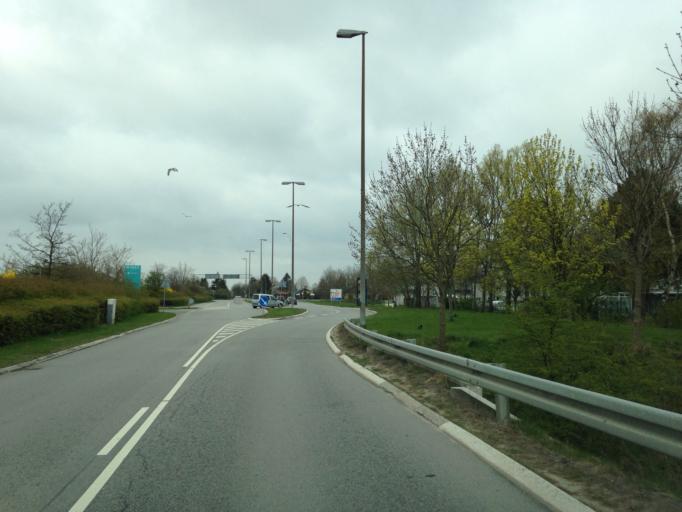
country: DK
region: Capital Region
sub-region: Ishoj Kommune
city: Ishoj
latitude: 55.6004
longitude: 12.3275
